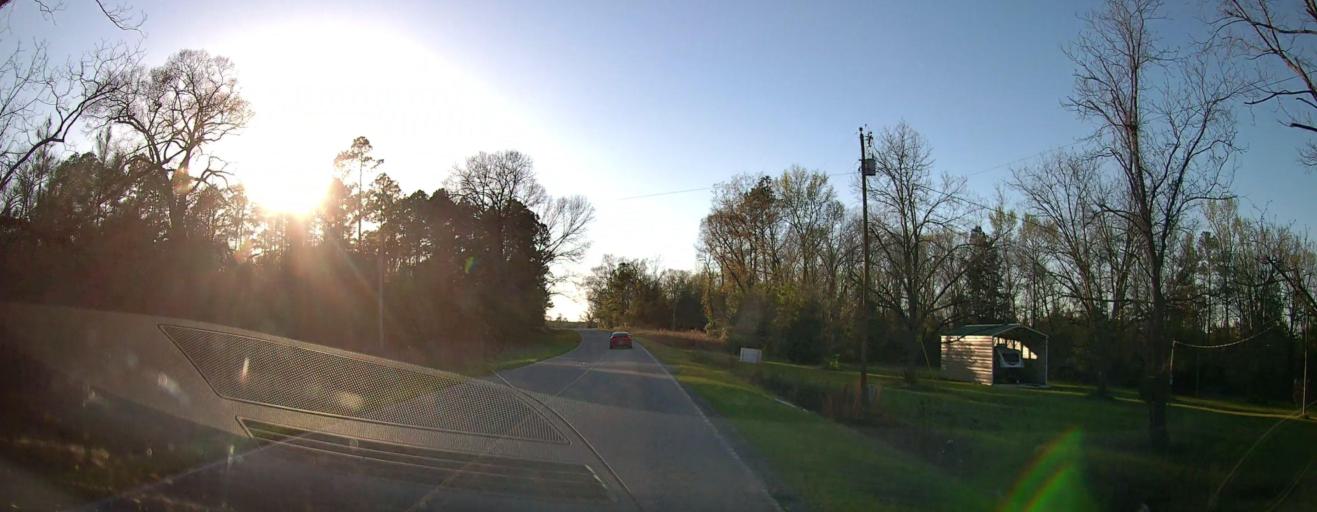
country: US
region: Georgia
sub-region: Wilkinson County
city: Gordon
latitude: 32.8769
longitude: -83.2524
